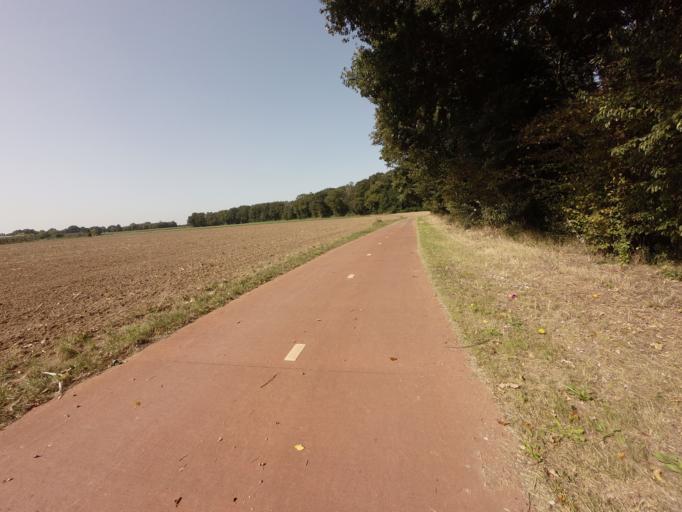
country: NL
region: Limburg
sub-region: Gemeente Roerdalen
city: Sint Odilienberg
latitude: 51.1438
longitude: 5.9895
